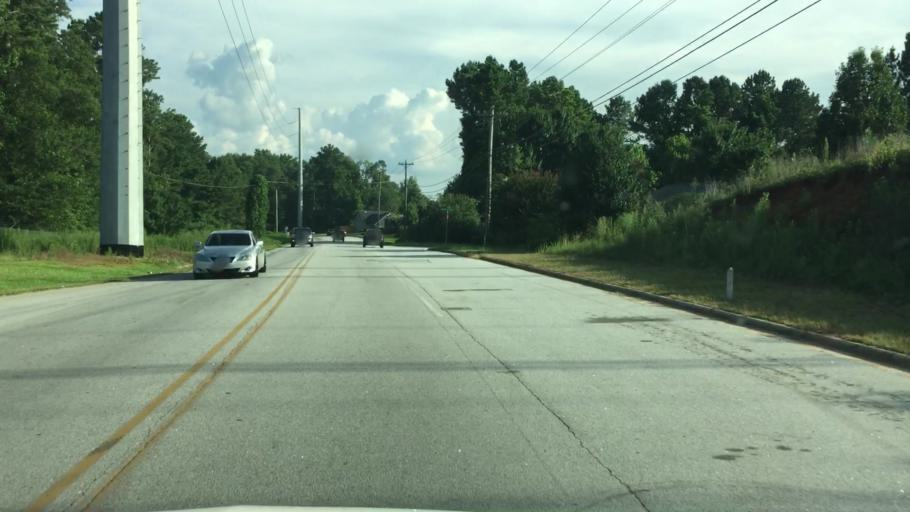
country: US
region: Georgia
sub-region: DeKalb County
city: Pine Mountain
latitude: 33.6383
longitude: -84.1294
